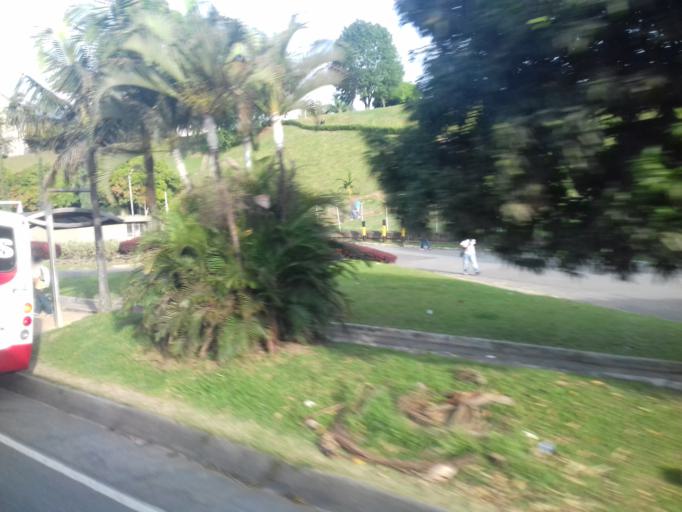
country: CO
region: Antioquia
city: Sabaneta
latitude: 6.1597
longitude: -75.6185
